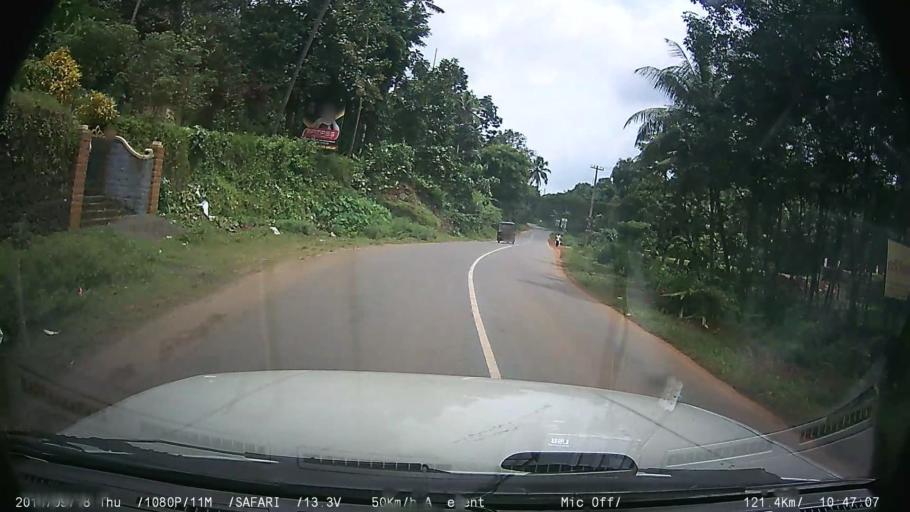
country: IN
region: Kerala
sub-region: Kottayam
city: Palackattumala
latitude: 9.7976
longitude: 76.5739
